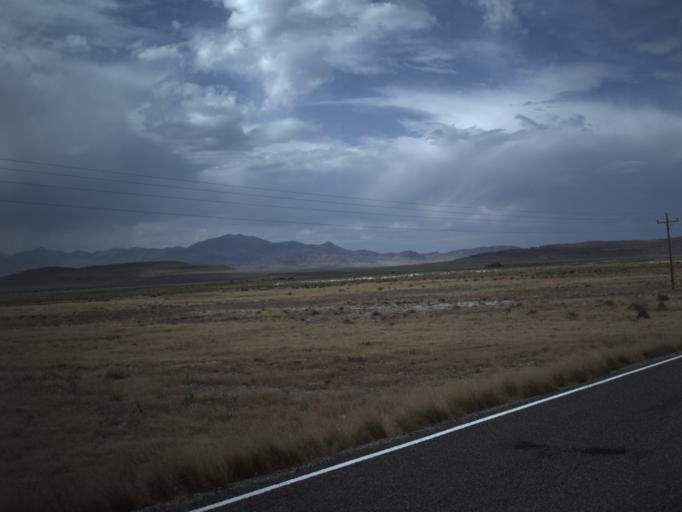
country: US
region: Utah
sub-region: Tooele County
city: Wendover
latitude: 41.4262
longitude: -113.8449
